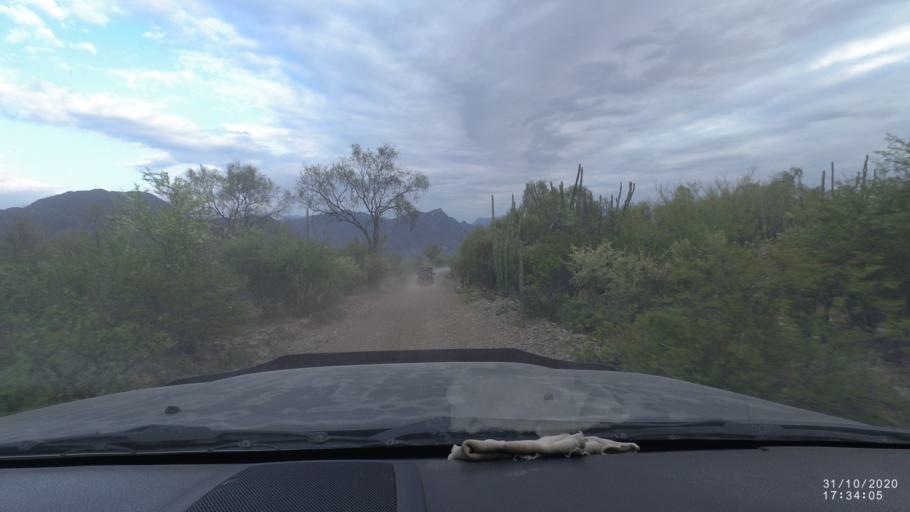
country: BO
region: Chuquisaca
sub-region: Provincia Zudanez
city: Mojocoya
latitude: -18.5999
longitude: -64.5487
